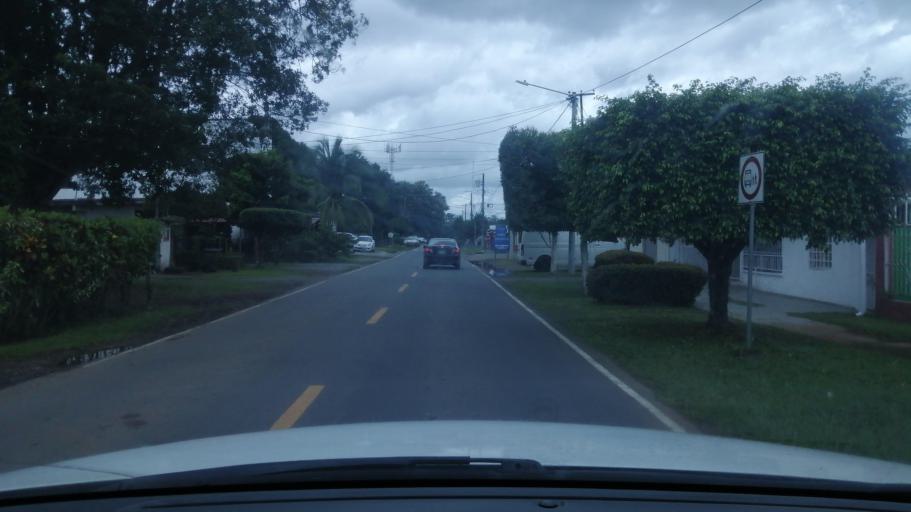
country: PA
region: Chiriqui
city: David
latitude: 8.4441
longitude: -82.4270
